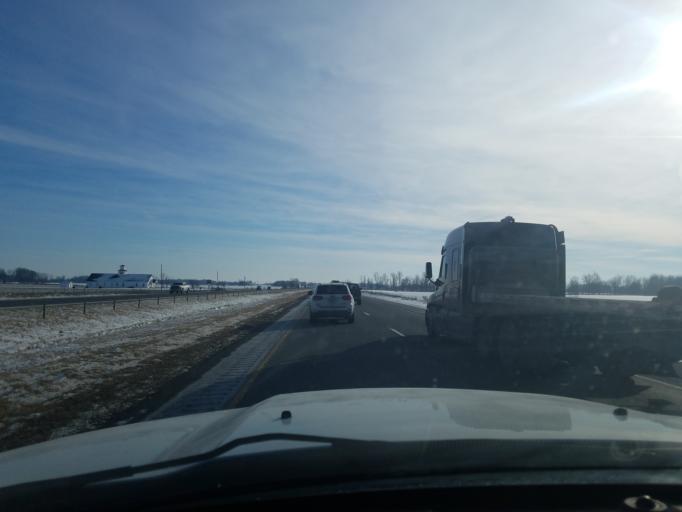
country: US
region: Indiana
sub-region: Madison County
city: Alexandria
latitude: 40.3215
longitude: -85.5589
